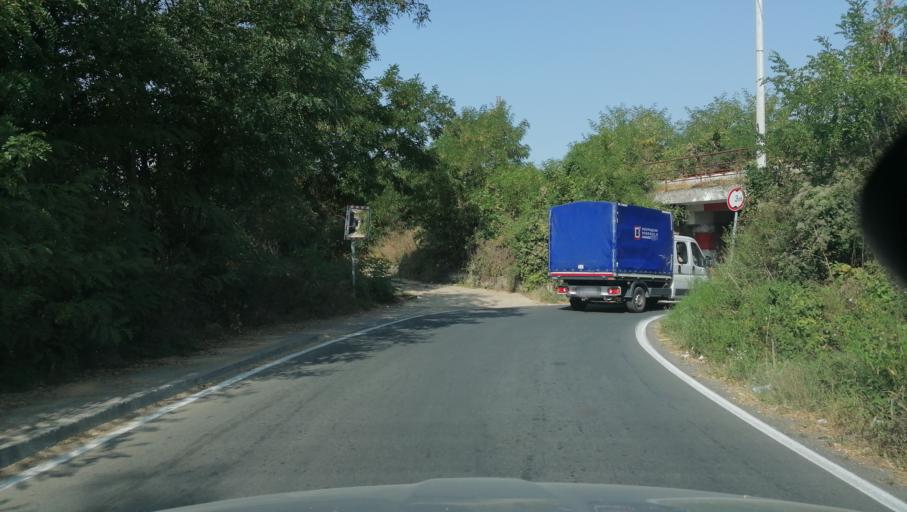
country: RS
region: Central Serbia
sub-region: Belgrade
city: Zvezdara
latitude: 44.7048
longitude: 20.5647
